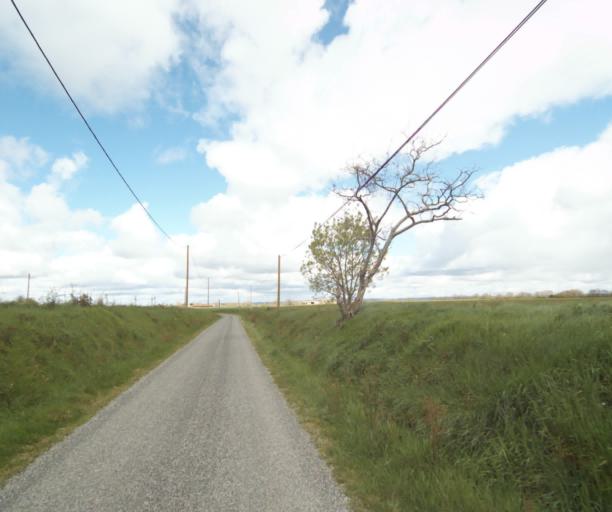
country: FR
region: Midi-Pyrenees
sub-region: Departement de l'Ariege
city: Saverdun
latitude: 43.2161
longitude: 1.5813
